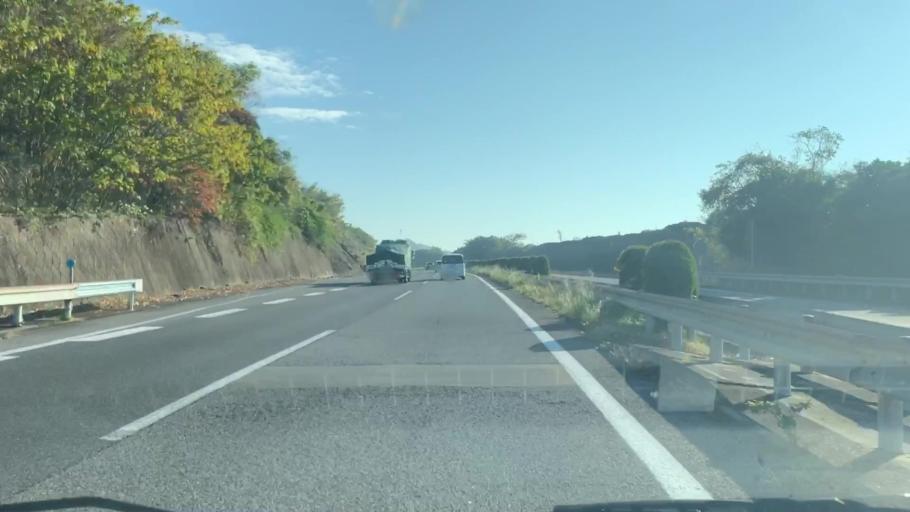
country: JP
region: Saga Prefecture
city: Saga-shi
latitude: 33.2866
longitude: 130.1521
